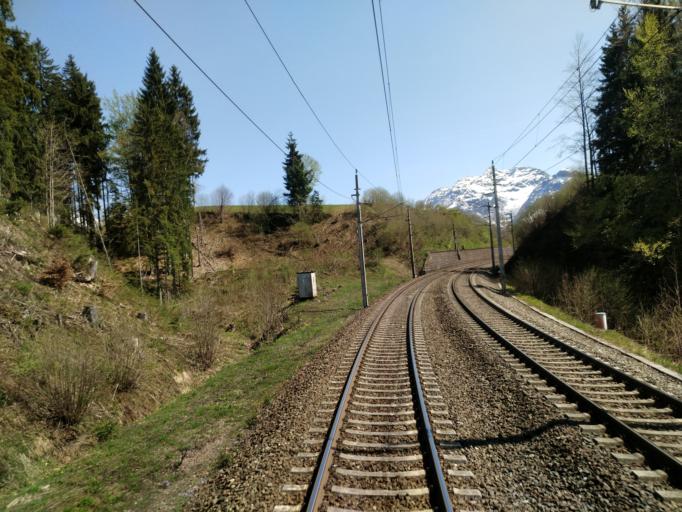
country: AT
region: Tyrol
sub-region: Politischer Bezirk Kitzbuhel
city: Fieberbrunn
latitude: 47.4734
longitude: 12.5628
